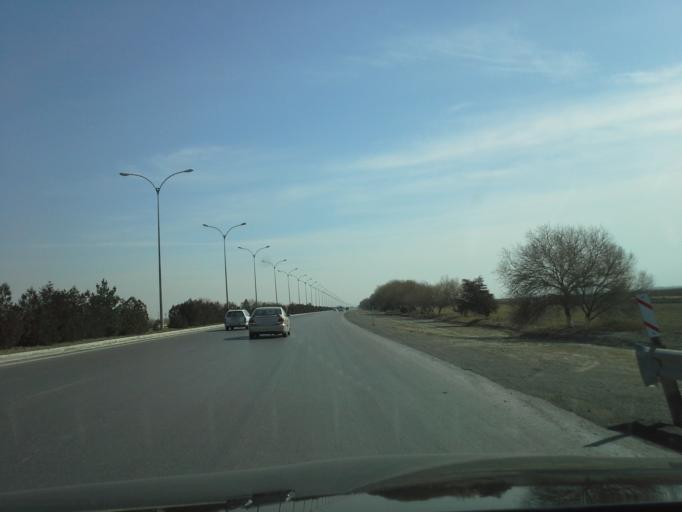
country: TM
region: Ahal
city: Abadan
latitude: 38.1335
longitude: 58.0171
